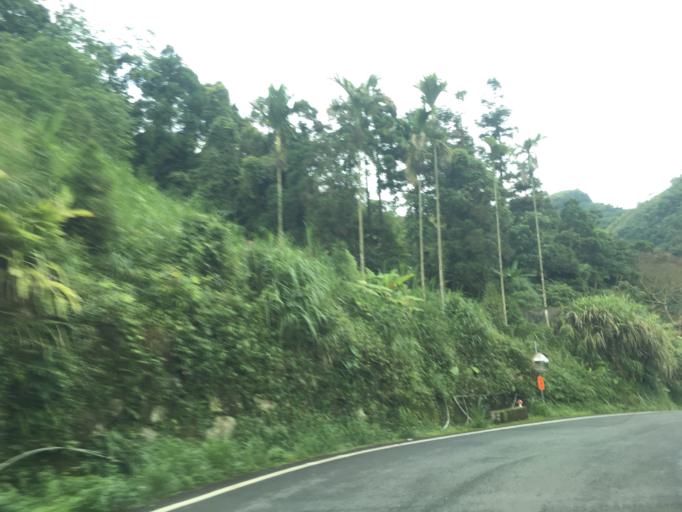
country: TW
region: Taiwan
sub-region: Chiayi
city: Jiayi Shi
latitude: 23.4475
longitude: 120.6647
